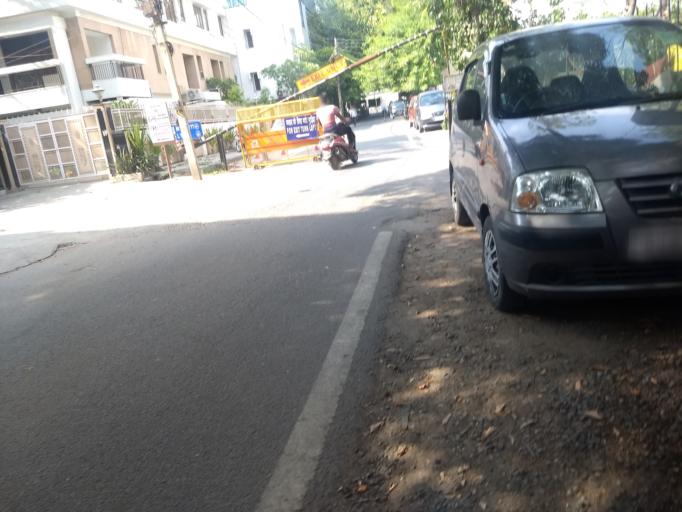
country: IN
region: NCT
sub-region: New Delhi
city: New Delhi
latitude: 28.5671
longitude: 77.2241
